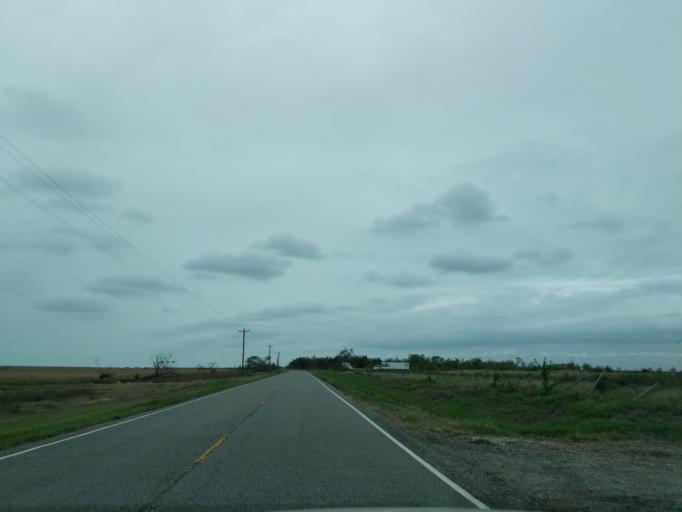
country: US
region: Louisiana
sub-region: Cameron Parish
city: Cameron
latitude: 29.7861
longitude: -93.1816
